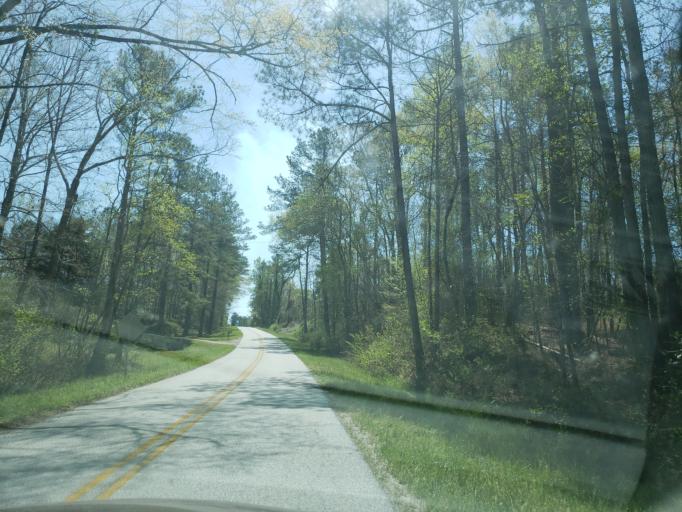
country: US
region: Alabama
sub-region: Elmore County
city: Tallassee
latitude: 32.6713
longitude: -85.8610
